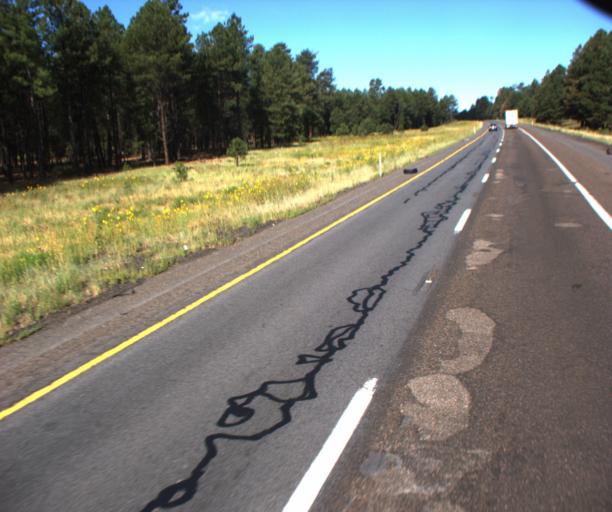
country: US
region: Arizona
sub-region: Coconino County
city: Parks
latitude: 35.2486
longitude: -111.8520
